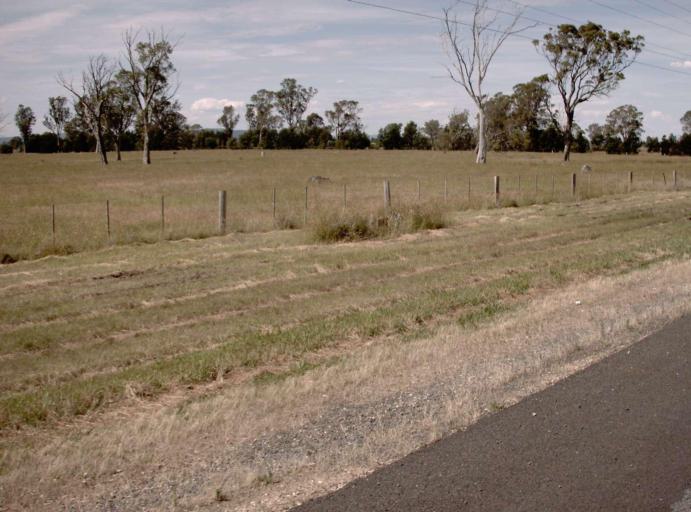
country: AU
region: Victoria
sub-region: East Gippsland
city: Bairnsdale
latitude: -37.8720
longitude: 147.4636
